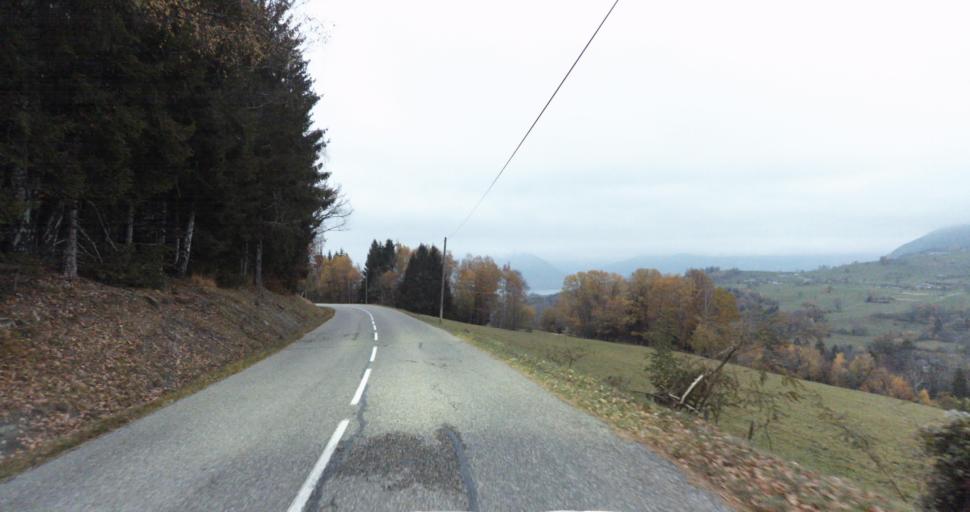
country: FR
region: Rhone-Alpes
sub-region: Departement de la Haute-Savoie
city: Saint-Jorioz
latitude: 45.8015
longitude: 6.1385
